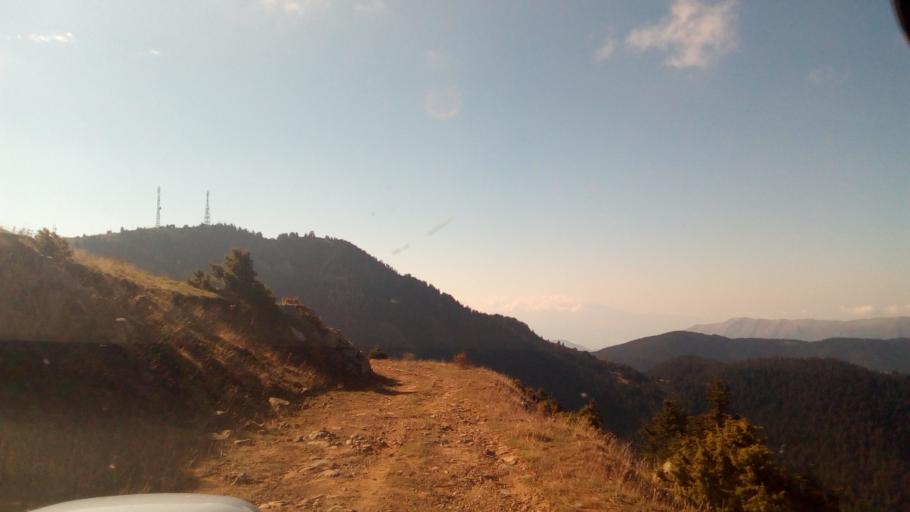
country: GR
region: Central Greece
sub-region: Nomos Fokidos
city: Lidoriki
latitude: 38.6112
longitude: 21.9629
